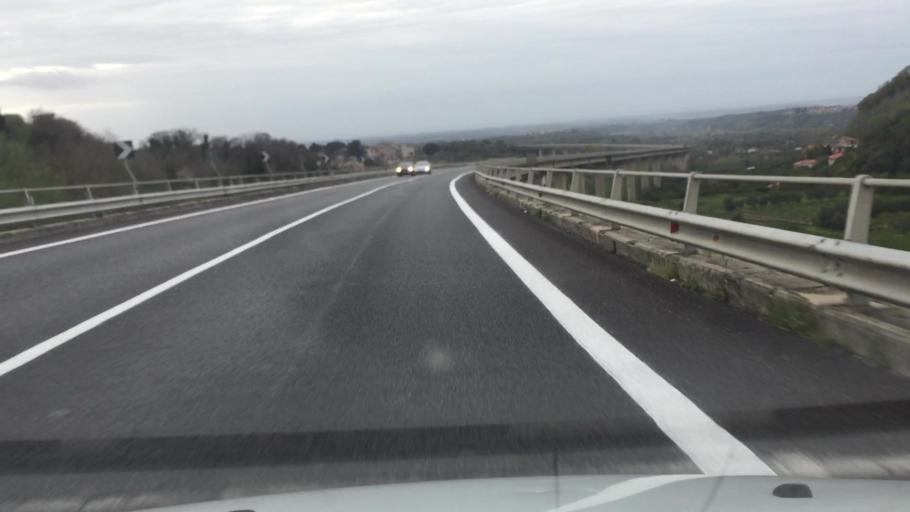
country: IT
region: Calabria
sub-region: Provincia di Reggio Calabria
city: Anoia Superiore
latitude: 38.4170
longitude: 16.1065
